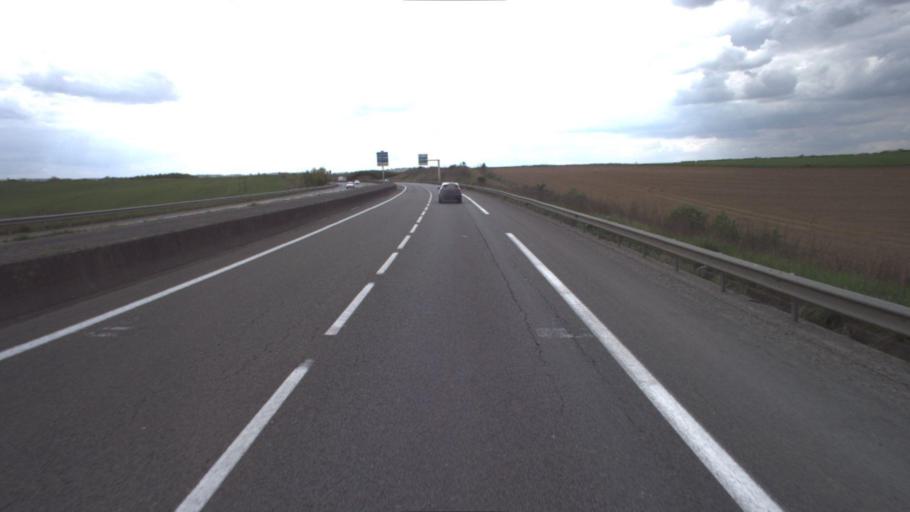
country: FR
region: Ile-de-France
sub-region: Departement de Seine-et-Marne
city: Villenoy
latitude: 48.9438
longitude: 2.8511
